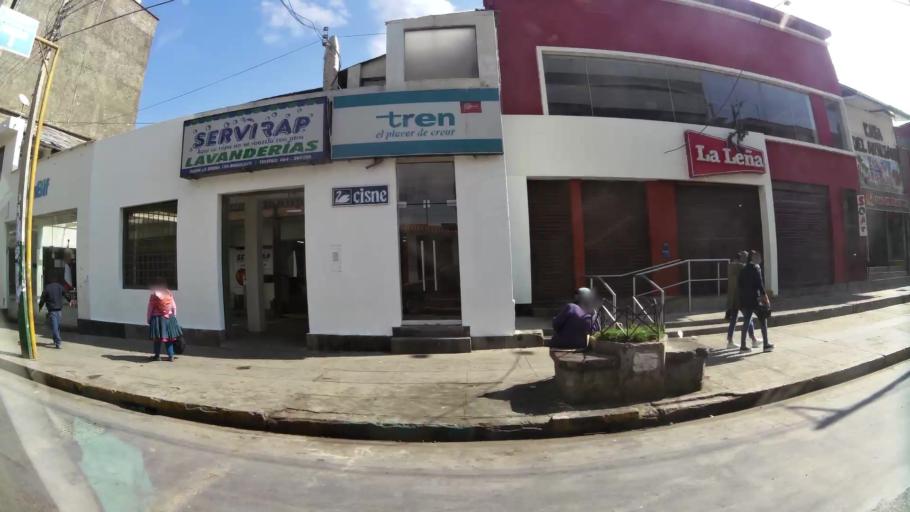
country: PE
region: Junin
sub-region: Provincia de Huancayo
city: El Tambo
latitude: -12.0689
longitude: -75.2108
